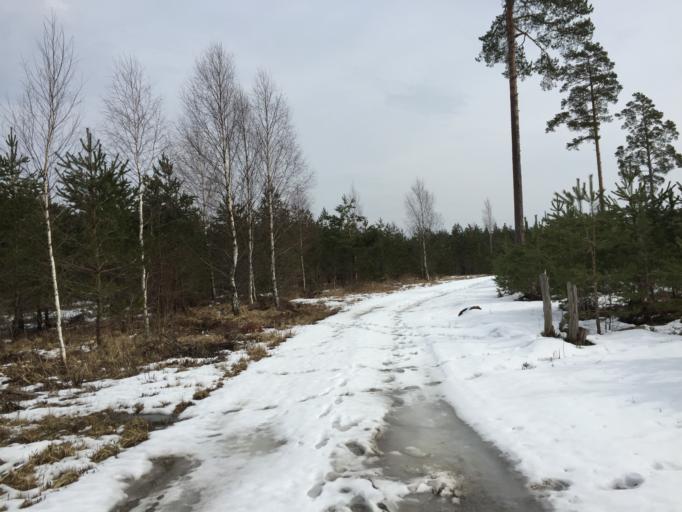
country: EE
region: Saare
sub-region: Kuressaare linn
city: Kuressaare
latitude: 58.3955
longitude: 22.1710
